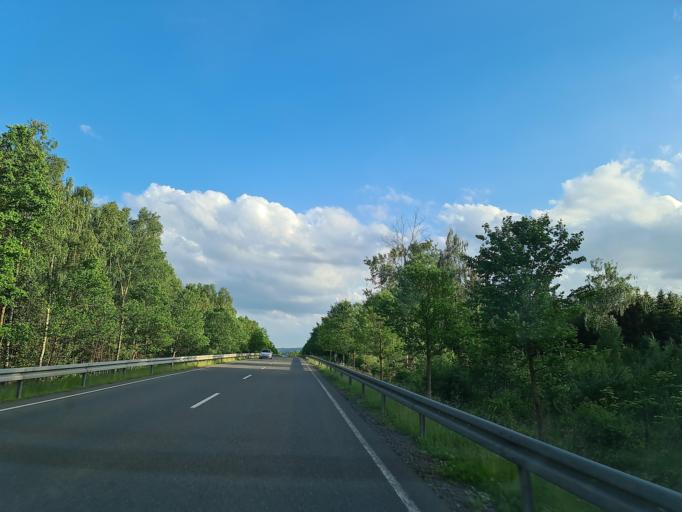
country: DE
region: Thuringia
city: Pormitz
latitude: 50.6312
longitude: 11.8146
